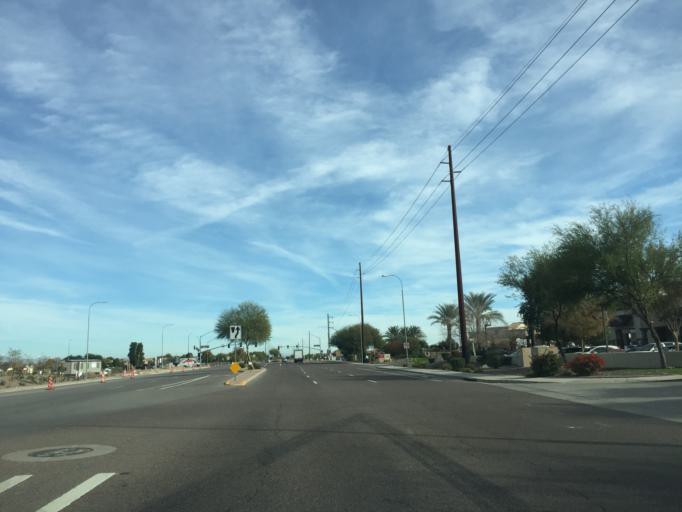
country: US
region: Arizona
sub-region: Maricopa County
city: Chandler
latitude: 33.2628
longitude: -111.7919
